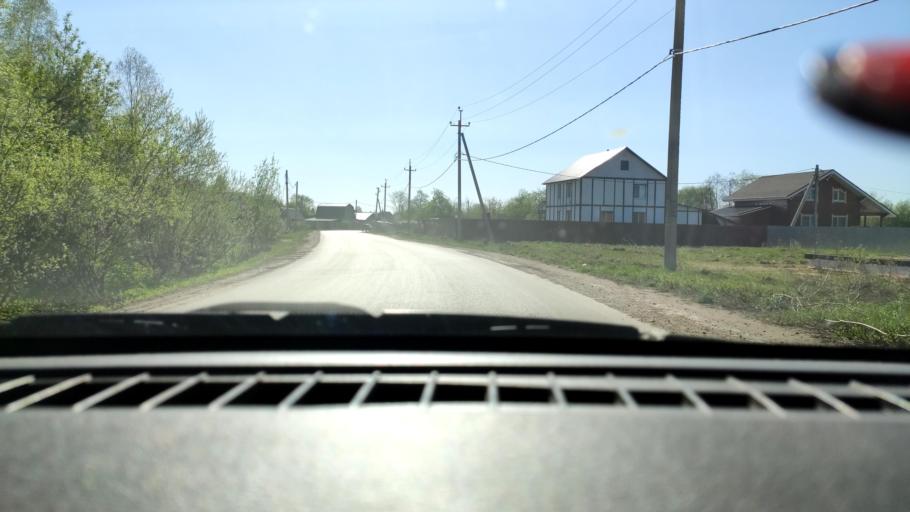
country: RU
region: Perm
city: Overyata
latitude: 58.0785
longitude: 55.9876
